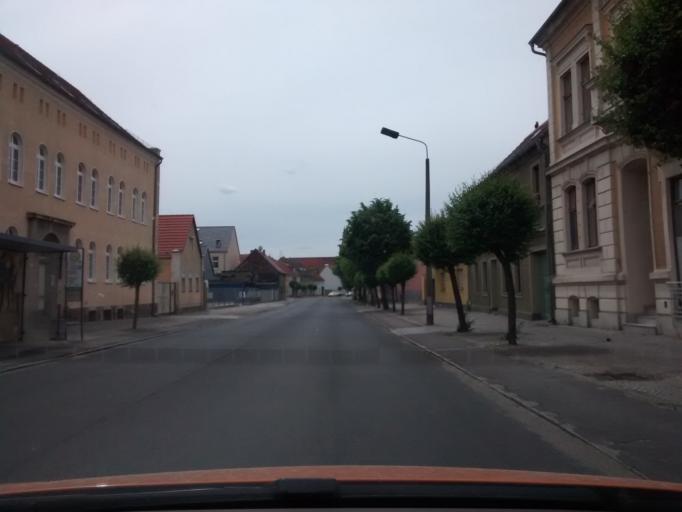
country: DE
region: Brandenburg
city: Juterbog
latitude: 51.9970
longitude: 13.0860
